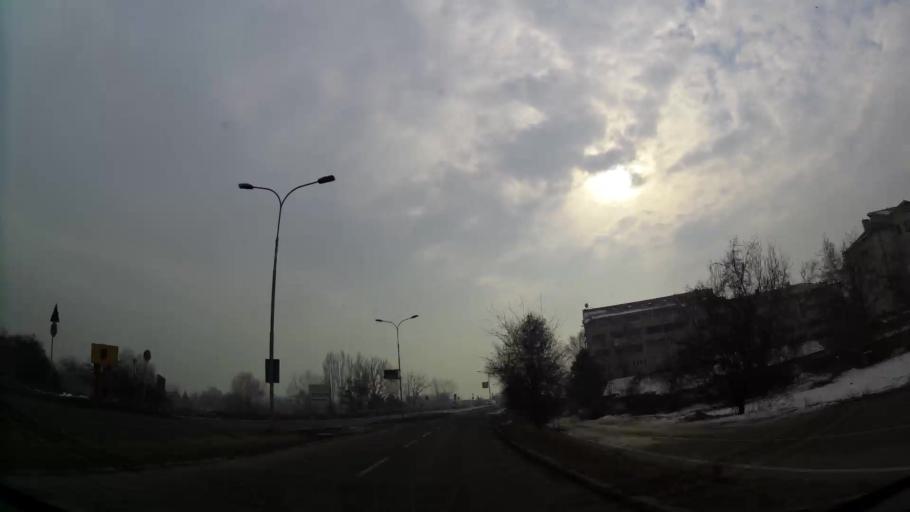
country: MK
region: Cair
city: Cair
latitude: 42.0041
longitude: 21.4701
